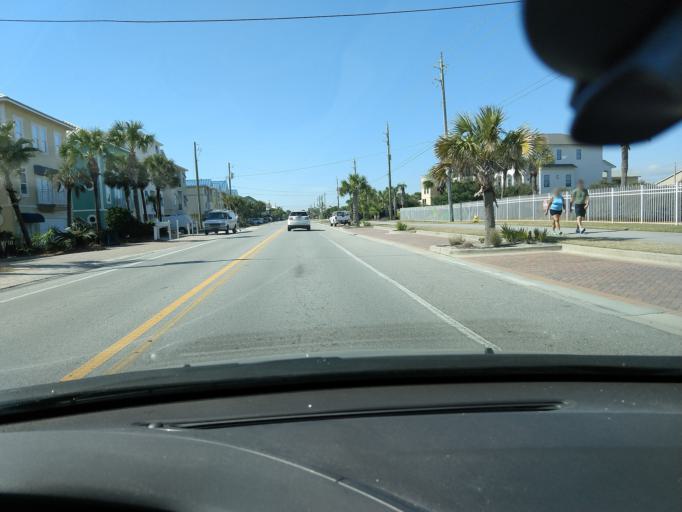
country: US
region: Florida
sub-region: Walton County
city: Miramar Beach
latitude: 30.3763
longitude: -86.3726
